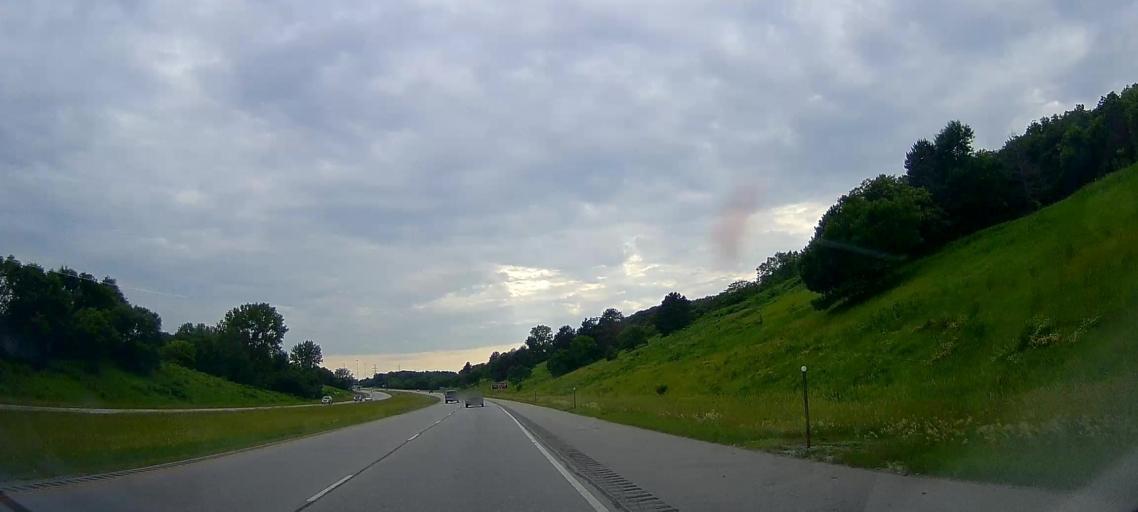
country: US
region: Iowa
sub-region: Pottawattamie County
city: Carter Lake
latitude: 41.3461
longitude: -96.0067
